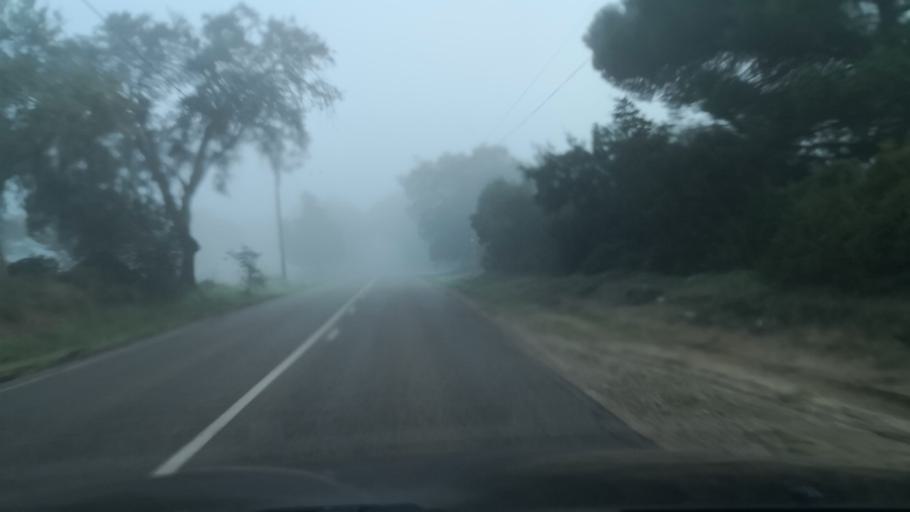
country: PT
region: Setubal
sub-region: Setubal
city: Setubal
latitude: 38.5495
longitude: -8.8468
